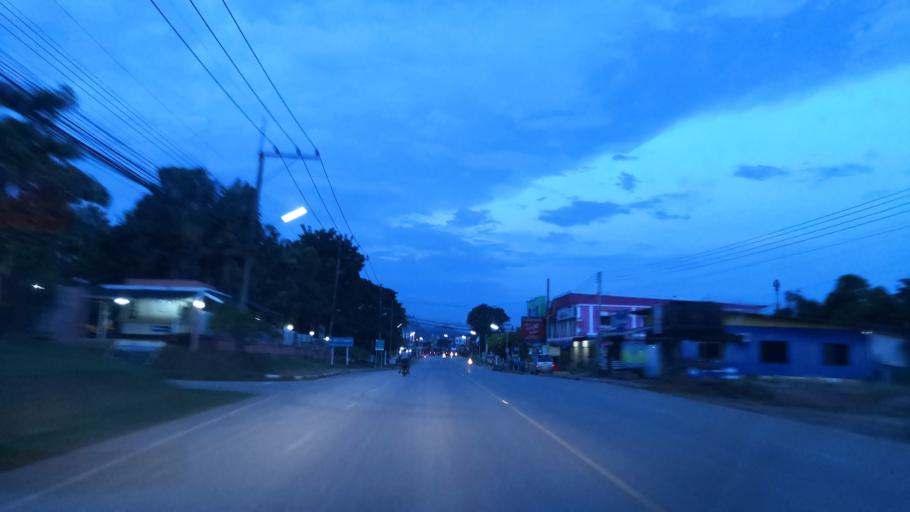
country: TH
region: Chiang Rai
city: Wiang Chiang Rung
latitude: 20.0018
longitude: 100.0406
